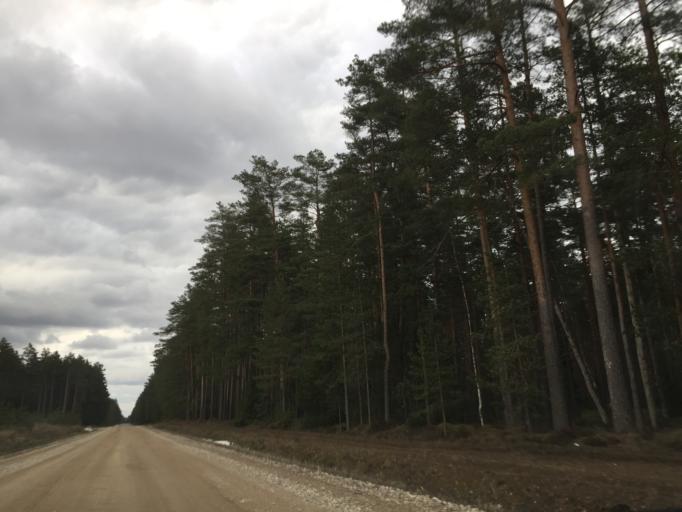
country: LV
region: Jaunjelgava
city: Jaunjelgava
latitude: 56.5763
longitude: 25.0190
